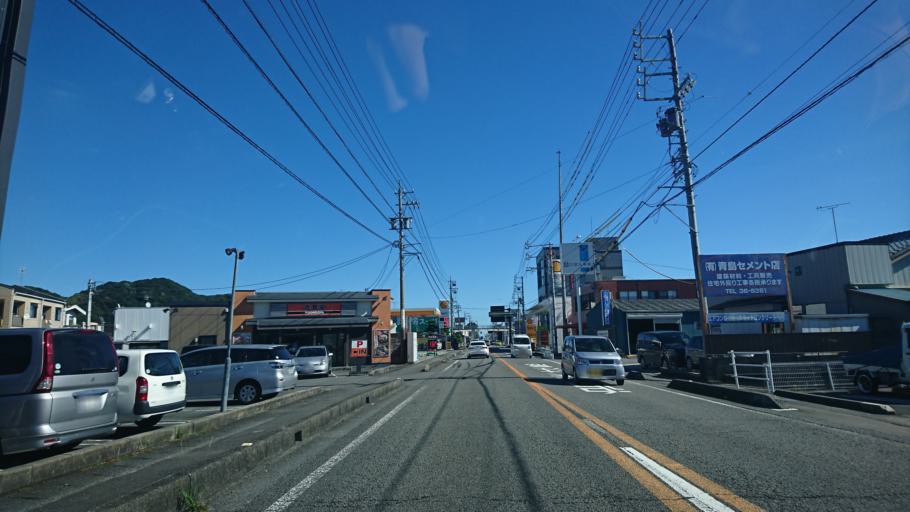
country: JP
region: Shizuoka
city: Shimada
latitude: 34.8377
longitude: 138.1805
